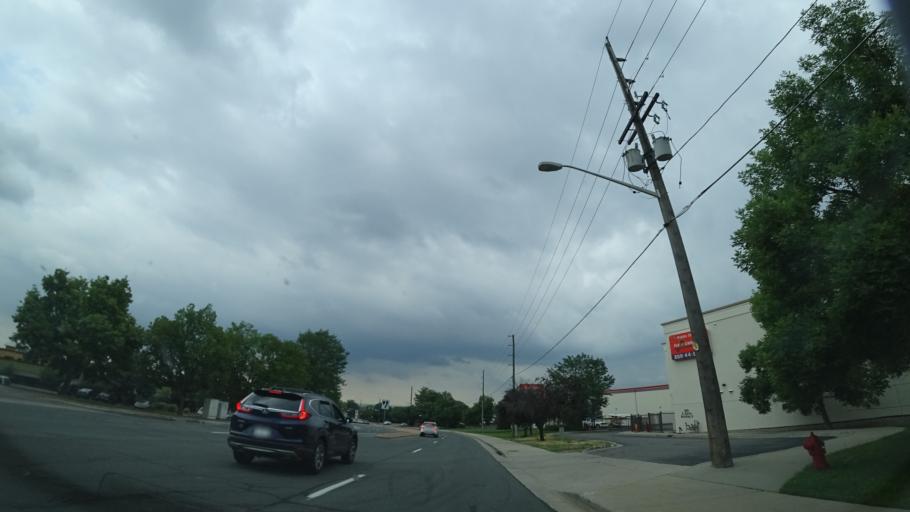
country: US
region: Colorado
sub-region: Jefferson County
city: West Pleasant View
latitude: 39.7120
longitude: -105.1355
